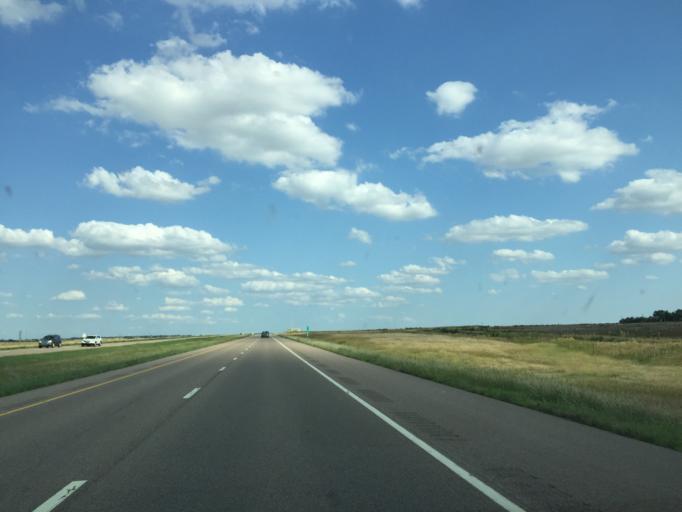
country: US
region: Kansas
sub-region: Gove County
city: Gove
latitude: 39.0847
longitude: -100.2990
